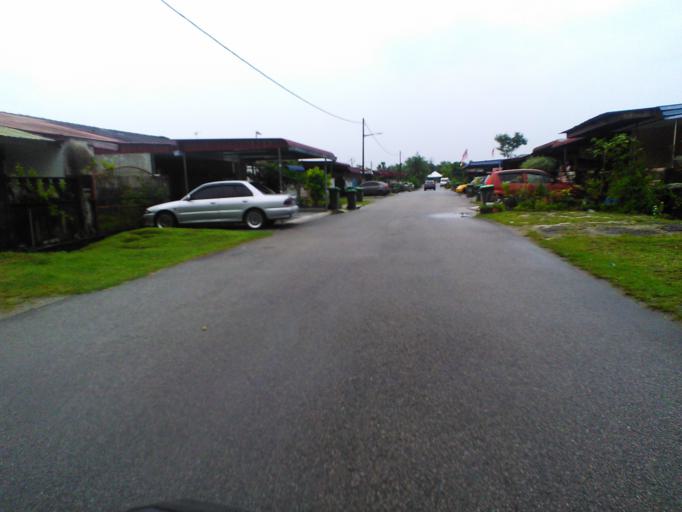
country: MY
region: Kedah
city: Kulim
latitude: 5.3624
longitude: 100.5741
